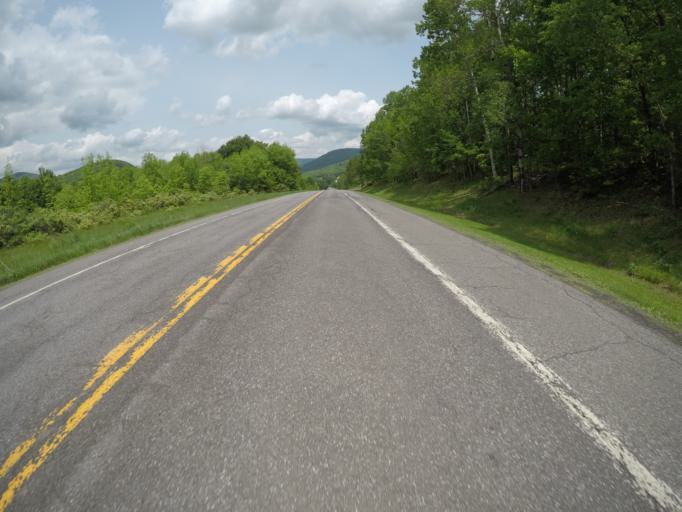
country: US
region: New York
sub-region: Delaware County
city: Stamford
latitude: 42.2637
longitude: -74.5860
